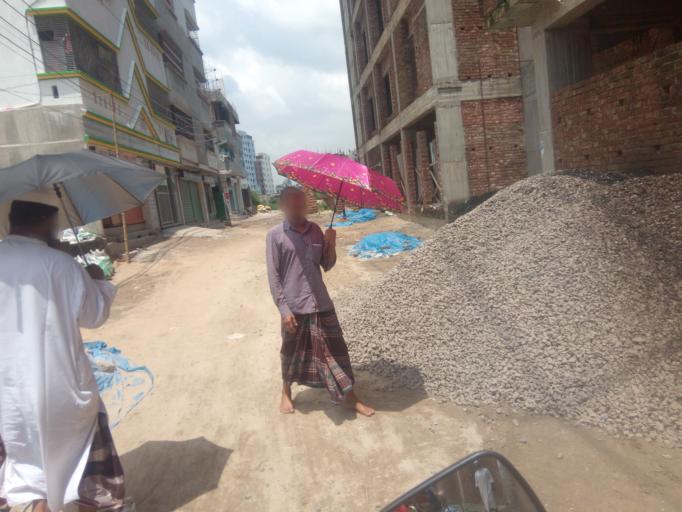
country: BD
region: Dhaka
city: Azimpur
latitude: 23.7514
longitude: 90.3502
